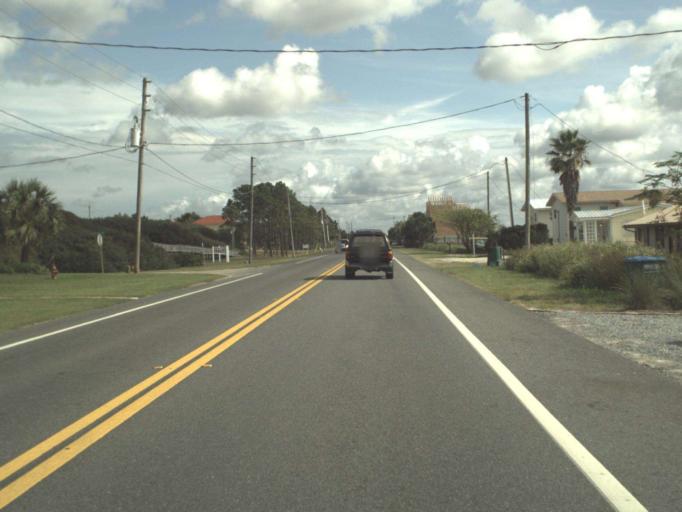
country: US
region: Florida
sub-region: Bay County
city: Mexico Beach
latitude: 29.9181
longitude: -85.3811
